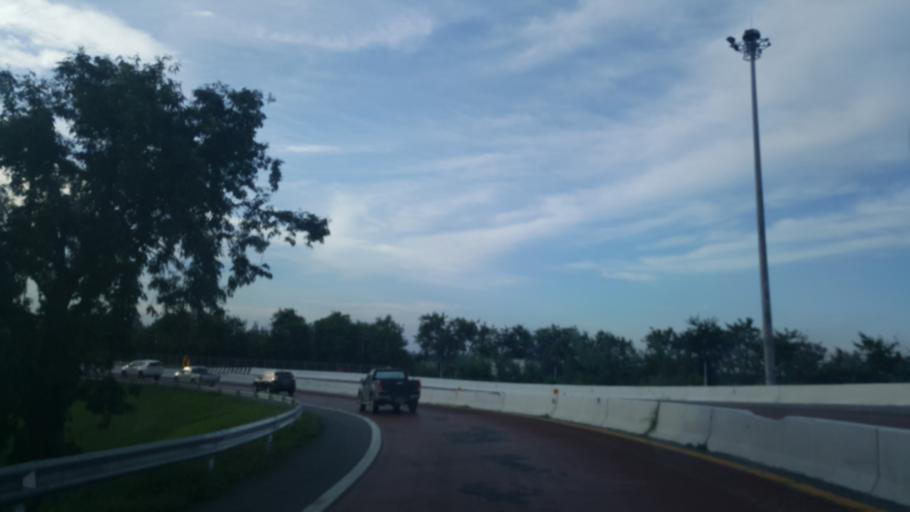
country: TH
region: Chachoengsao
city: Bang Pakong
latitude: 13.6012
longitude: 100.9539
